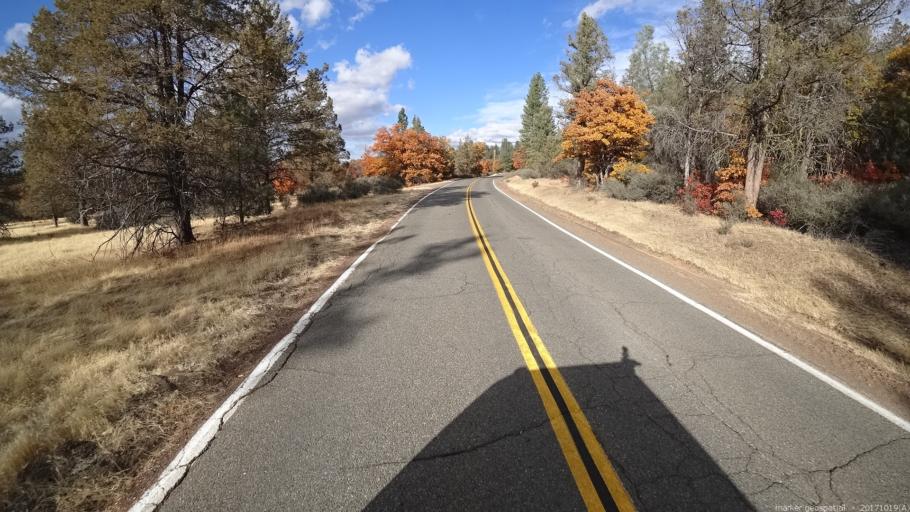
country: US
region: California
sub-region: Shasta County
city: Burney
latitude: 40.9853
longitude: -121.4333
